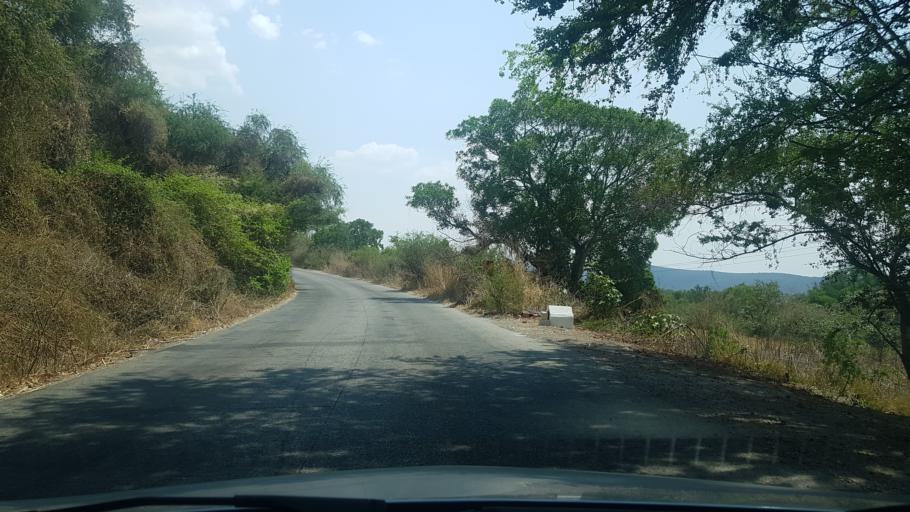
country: MX
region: Morelos
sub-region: Tlaltizapan de Zapata
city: Colonia Palo Prieto (Chipitongo)
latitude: 18.7508
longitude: -99.1138
